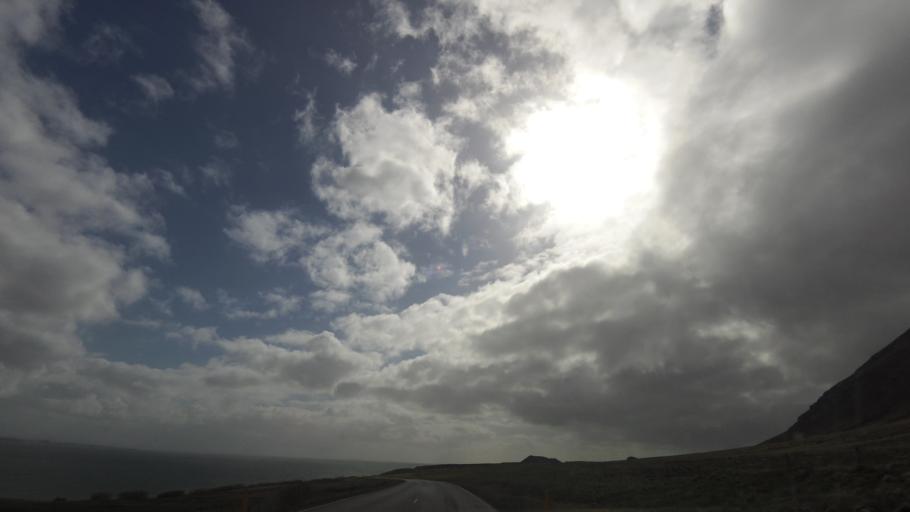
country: IS
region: Capital Region
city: Reykjavik
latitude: 64.3213
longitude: -21.8804
